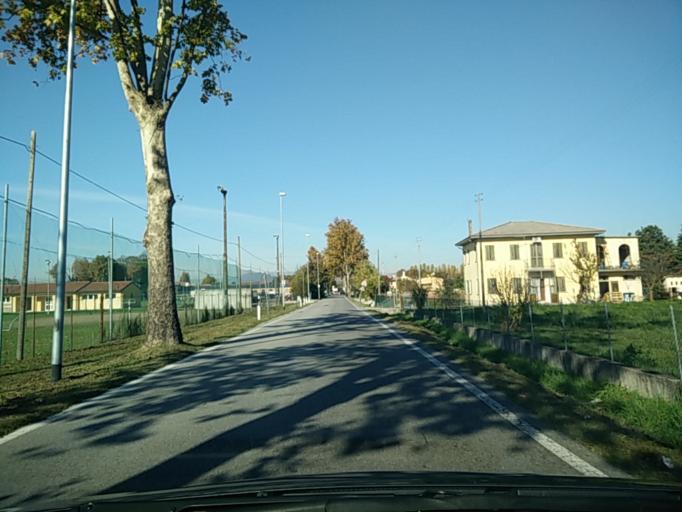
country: IT
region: Veneto
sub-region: Provincia di Treviso
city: Varago
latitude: 45.7190
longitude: 12.3049
